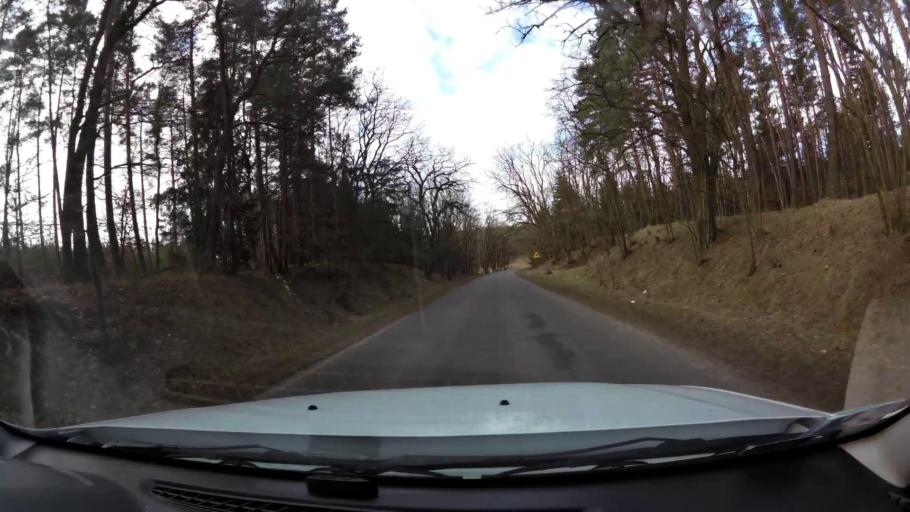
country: PL
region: West Pomeranian Voivodeship
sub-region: Powiat mysliborski
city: Debno
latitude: 52.8290
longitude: 14.6486
